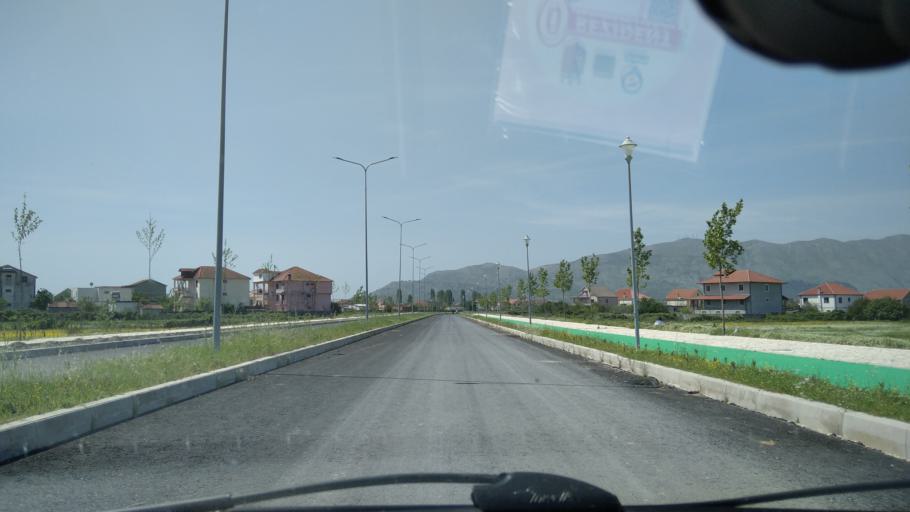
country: AL
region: Shkoder
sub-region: Rrethi i Shkodres
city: Shkoder
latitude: 42.0875
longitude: 19.5048
